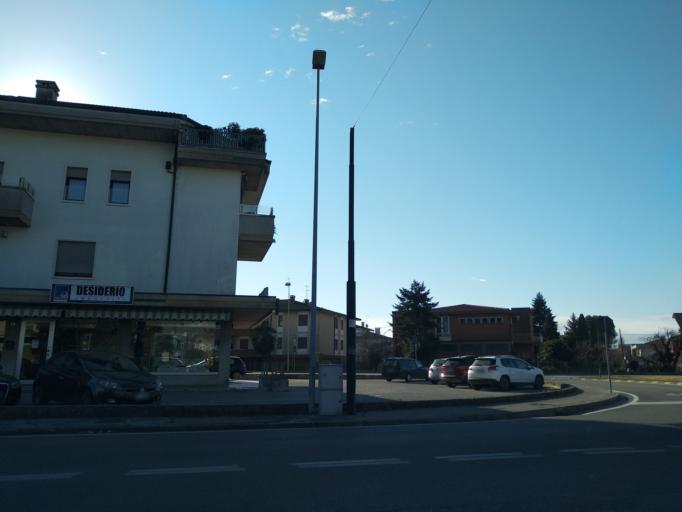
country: IT
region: Veneto
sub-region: Provincia di Vicenza
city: Camisano Vicentino
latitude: 45.5167
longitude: 11.7066
